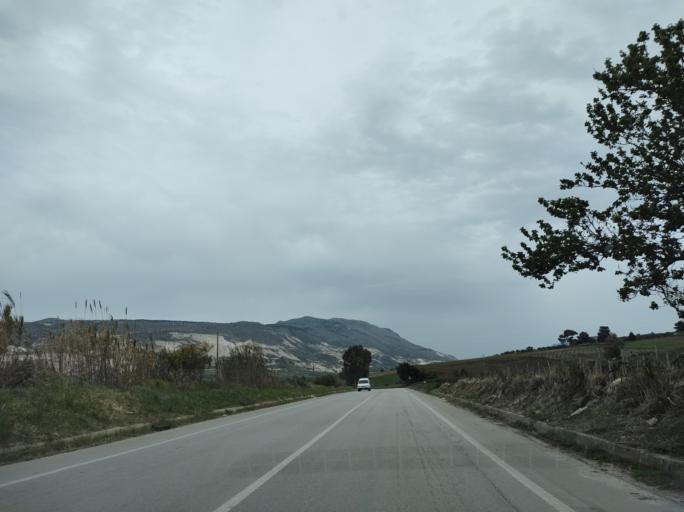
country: IT
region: Sicily
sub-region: Trapani
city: Custonaci
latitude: 38.0416
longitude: 12.6796
